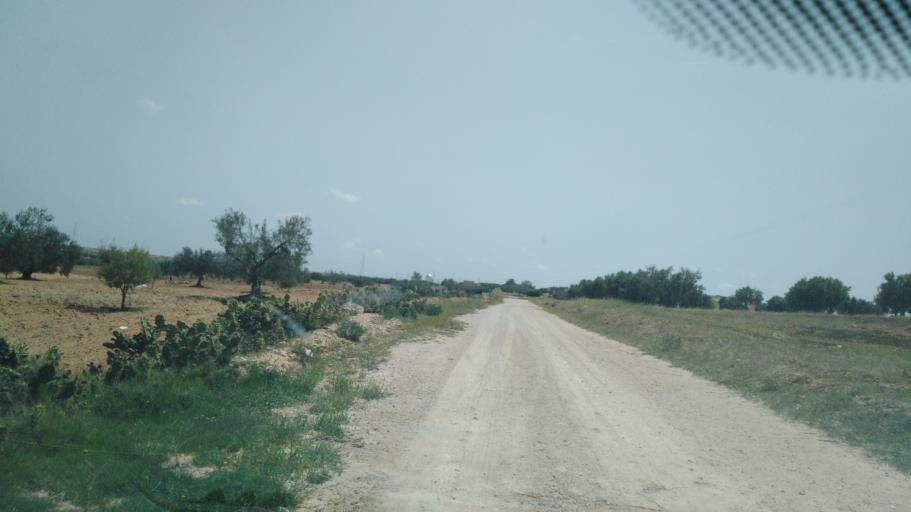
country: TN
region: Safaqis
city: Sfax
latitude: 34.7511
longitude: 10.5644
